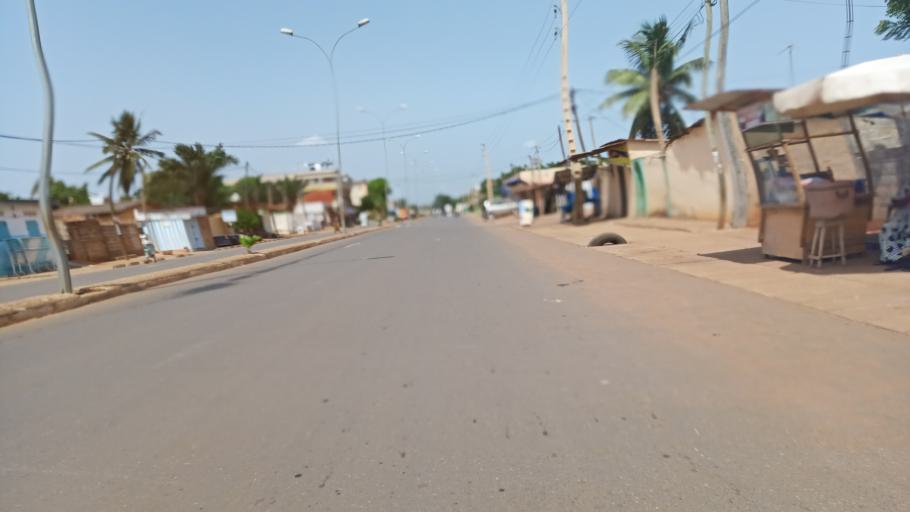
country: TG
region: Maritime
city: Lome
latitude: 6.2258
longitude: 1.1995
